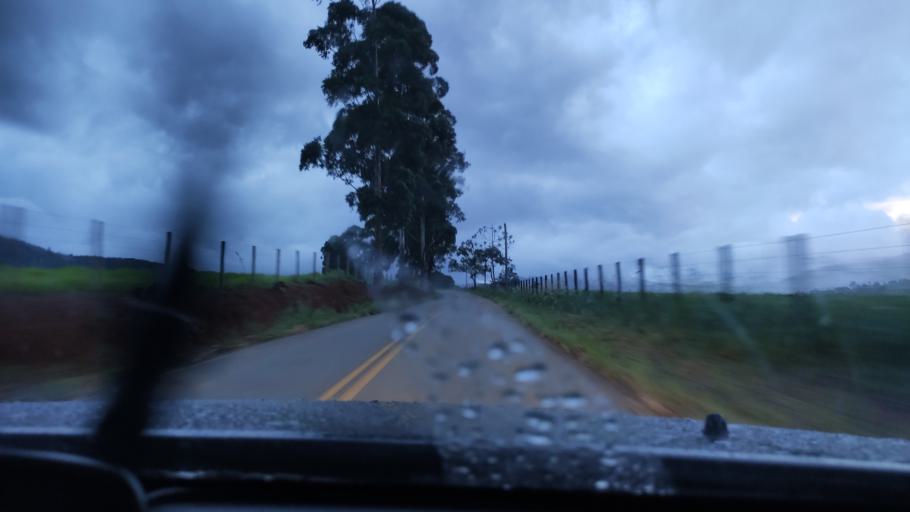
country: BR
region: Sao Paulo
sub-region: Serra Negra
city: Serra Negra
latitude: -22.5779
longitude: -46.6220
